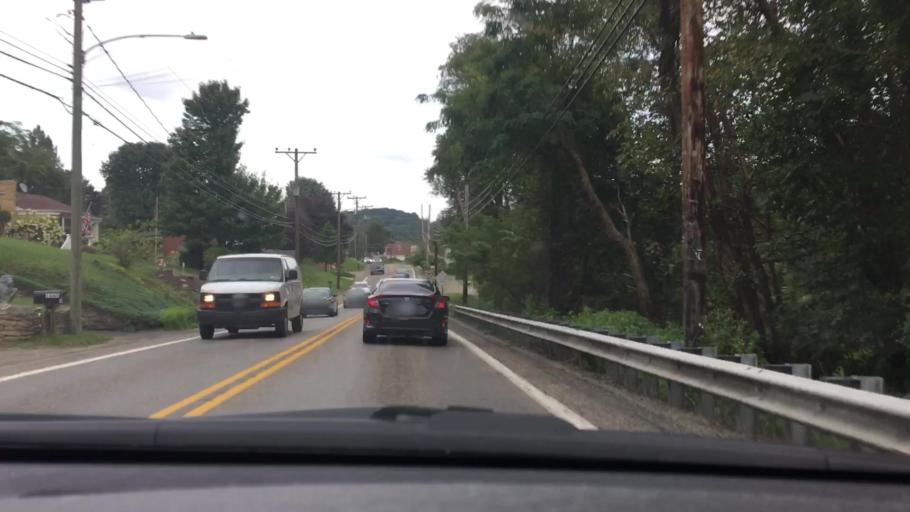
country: US
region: Pennsylvania
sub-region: Allegheny County
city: Baldwin
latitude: 40.3308
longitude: -79.9941
